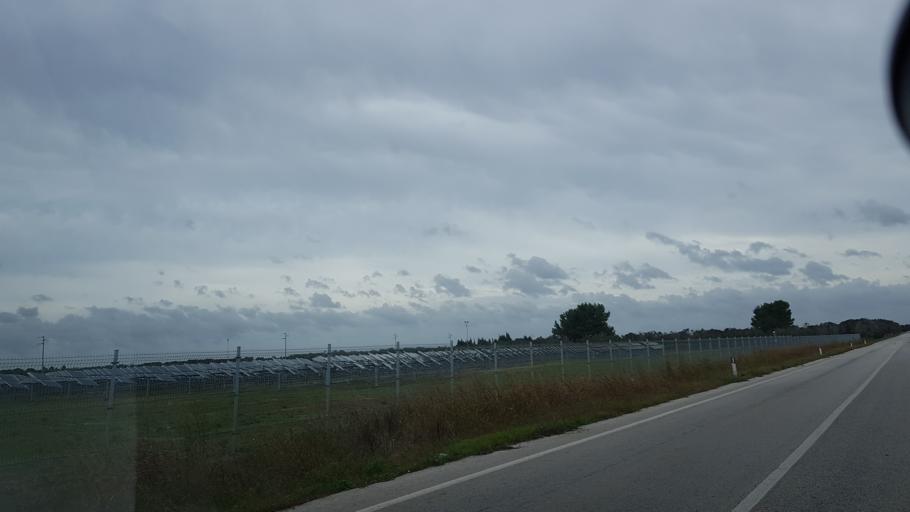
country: IT
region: Apulia
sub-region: Provincia di Lecce
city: Guagnano
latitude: 40.4002
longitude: 17.9152
